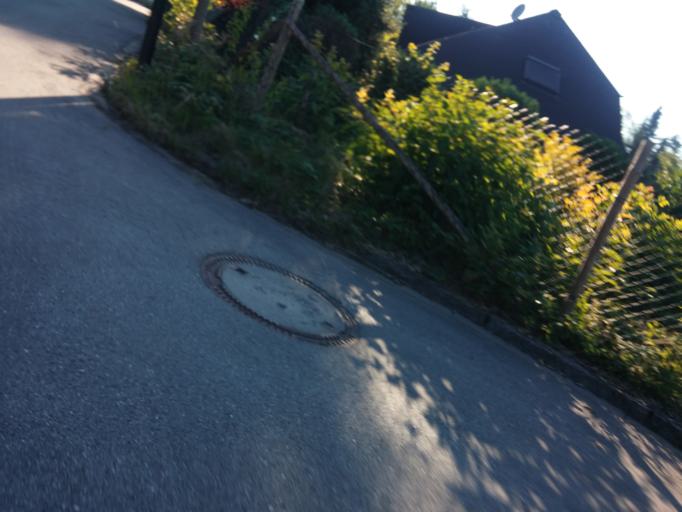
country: DE
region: Bavaria
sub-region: Upper Bavaria
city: Vaterstetten
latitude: 48.0988
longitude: 11.7966
